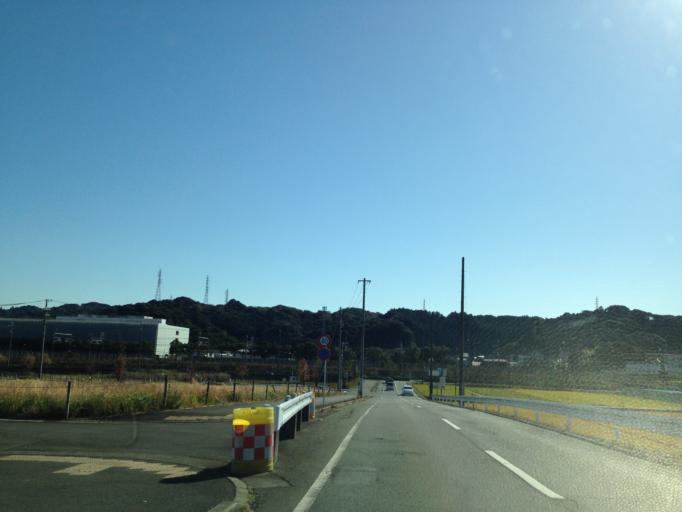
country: JP
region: Shizuoka
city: Fukuroi
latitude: 34.7520
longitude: 137.9540
